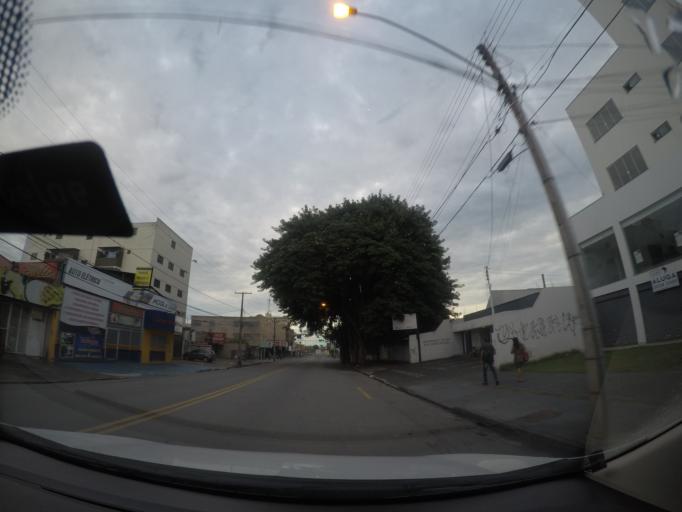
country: BR
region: Goias
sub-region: Goiania
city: Goiania
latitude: -16.6770
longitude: -49.2853
